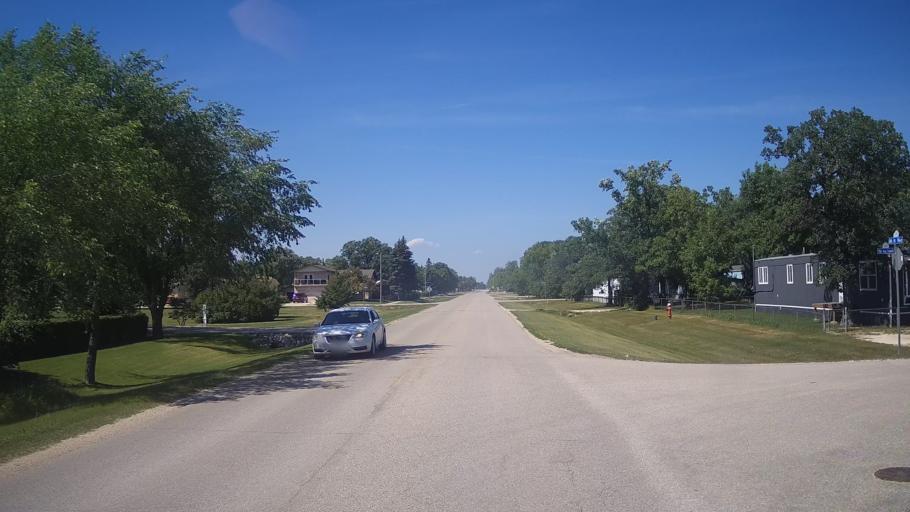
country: CA
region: Manitoba
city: Stonewall
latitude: 50.1259
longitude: -97.3333
